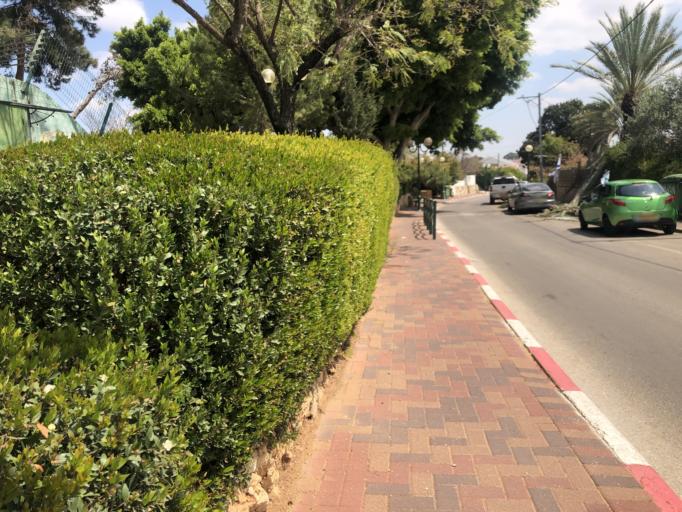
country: IL
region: Central District
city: Kfar Saba
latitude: 32.1541
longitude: 34.9154
